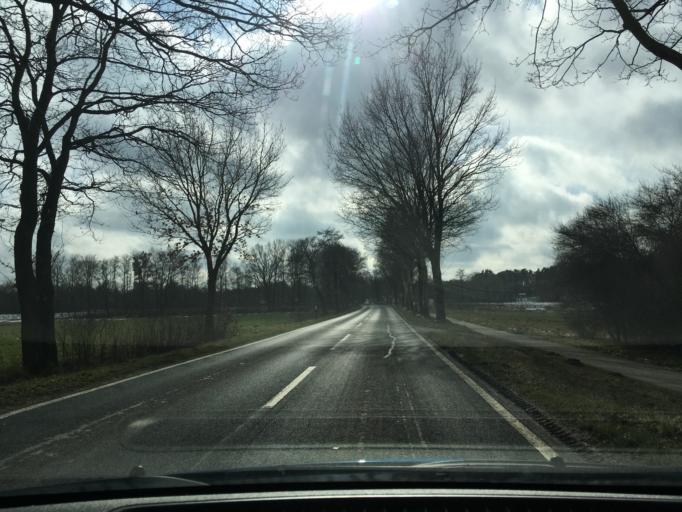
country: DE
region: Lower Saxony
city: Barum
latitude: 53.3407
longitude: 10.4020
